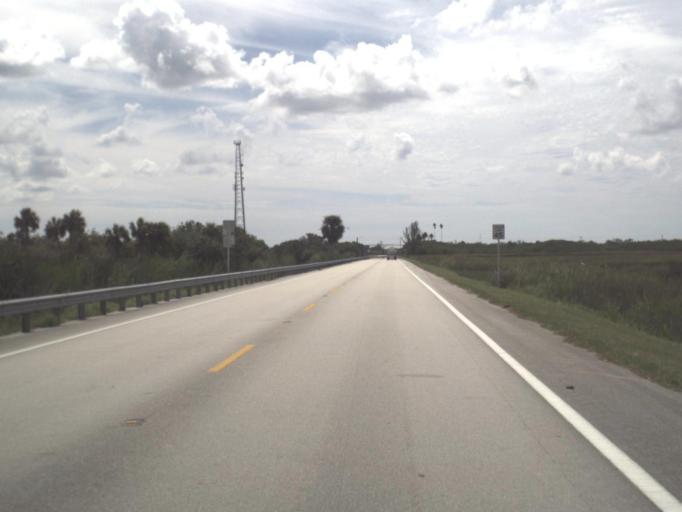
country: US
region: Florida
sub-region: Collier County
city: Marco
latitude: 25.9160
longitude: -81.3613
